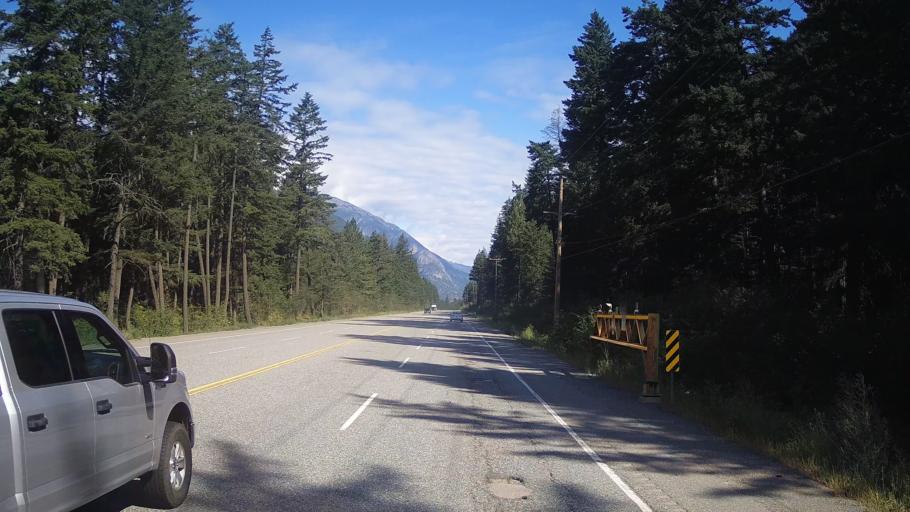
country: CA
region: British Columbia
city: Hope
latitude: 50.0389
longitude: -121.5347
